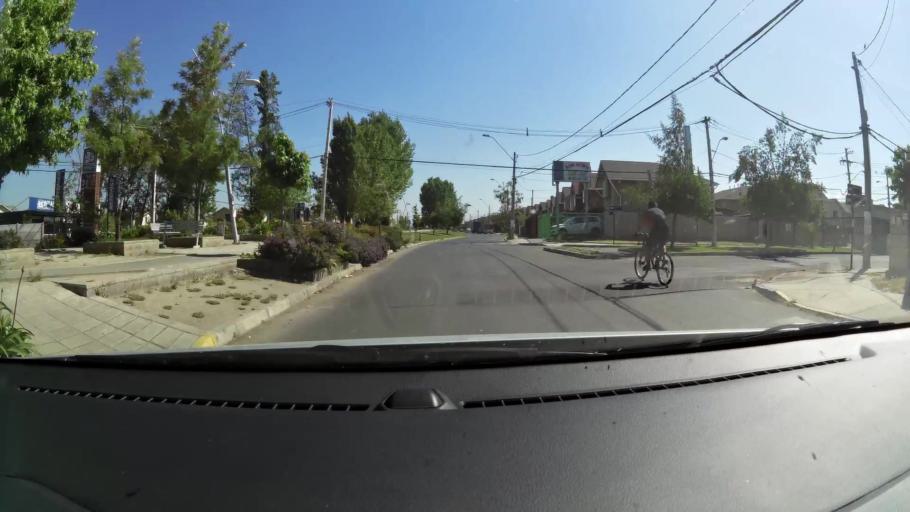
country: CL
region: Santiago Metropolitan
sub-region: Provincia de Maipo
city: San Bernardo
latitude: -33.6130
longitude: -70.6881
